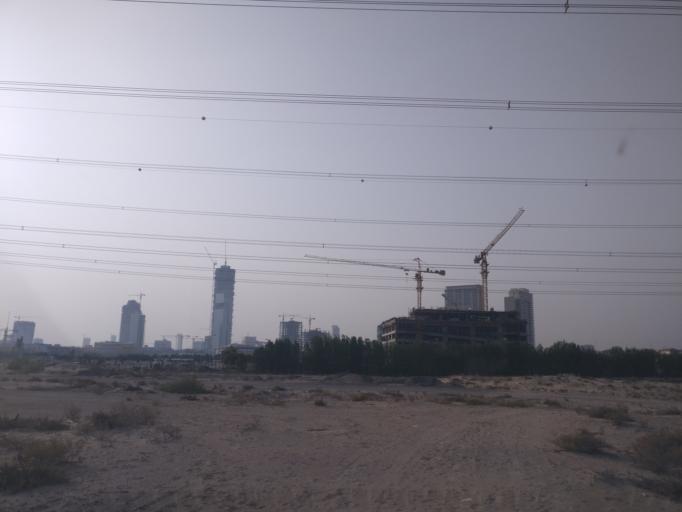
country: AE
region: Dubai
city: Dubai
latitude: 25.0600
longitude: 55.1926
